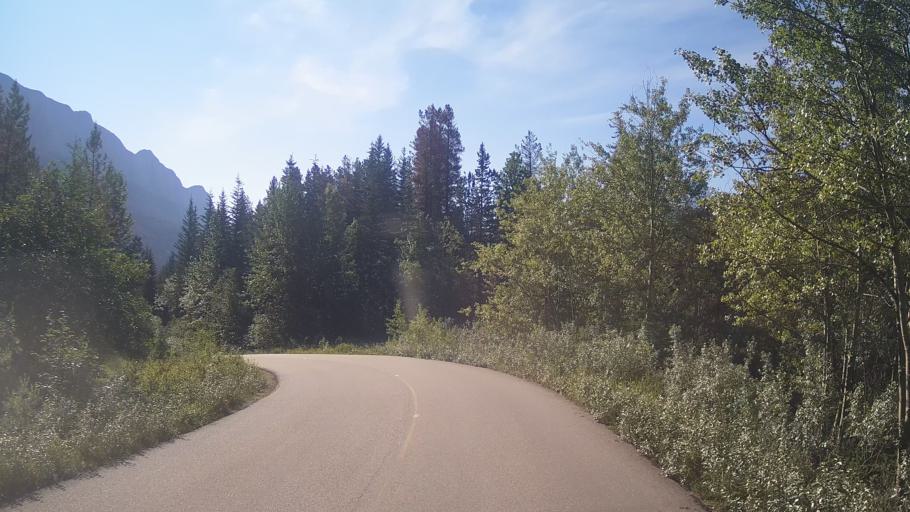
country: CA
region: Alberta
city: Hinton
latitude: 53.1774
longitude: -117.8444
